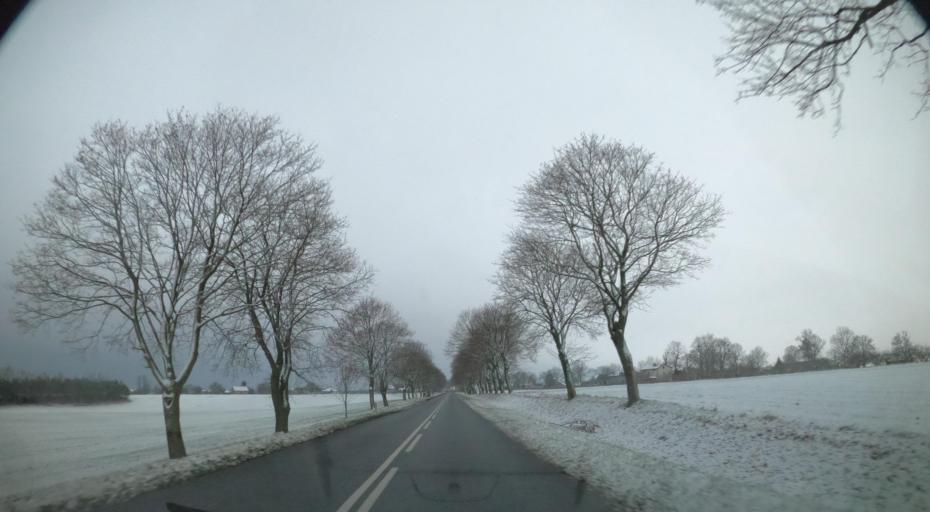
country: PL
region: Kujawsko-Pomorskie
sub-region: Powiat lipnowski
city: Dobrzyn nad Wisla
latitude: 52.6466
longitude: 19.3474
